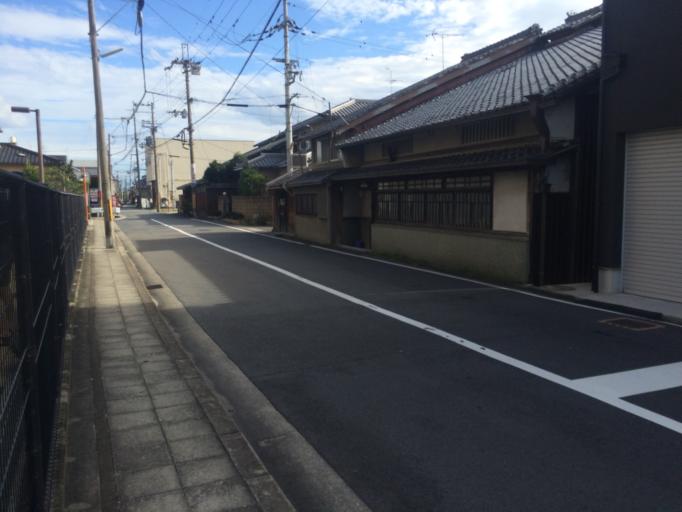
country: JP
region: Nara
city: Nara-shi
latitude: 34.6737
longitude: 135.8306
